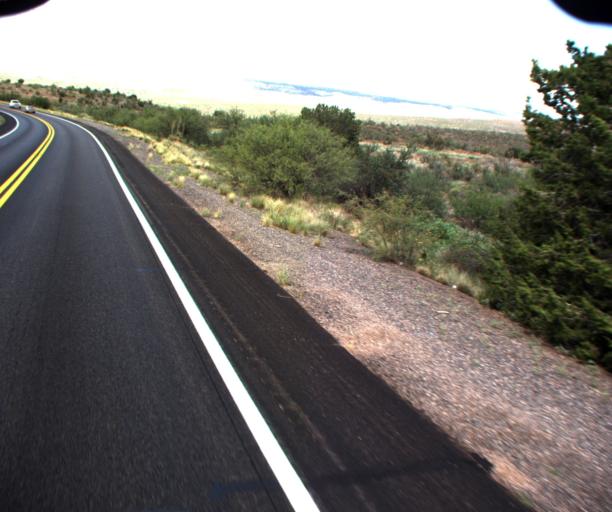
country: US
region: Arizona
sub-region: Yavapai County
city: Camp Verde
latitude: 34.5104
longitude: -111.7418
